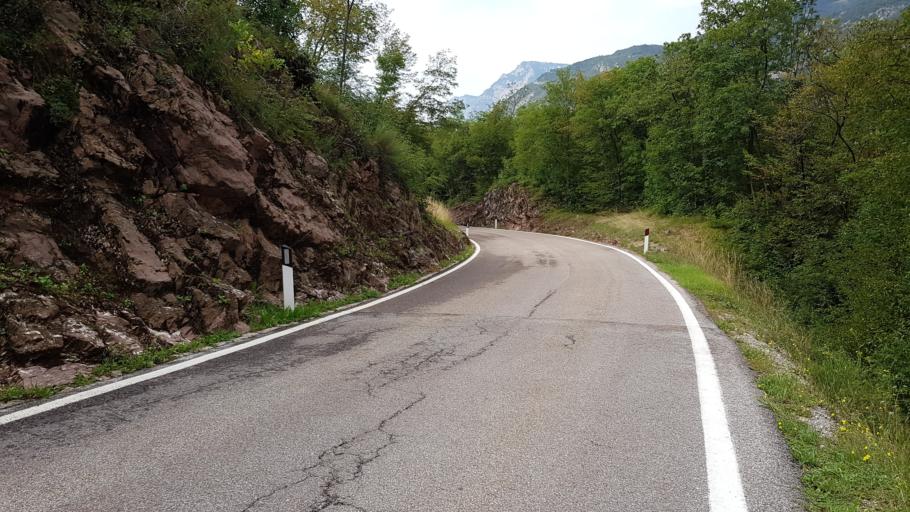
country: IT
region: Trentino-Alto Adige
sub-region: Provincia di Trento
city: Vezzano
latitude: 46.0826
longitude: 10.9947
